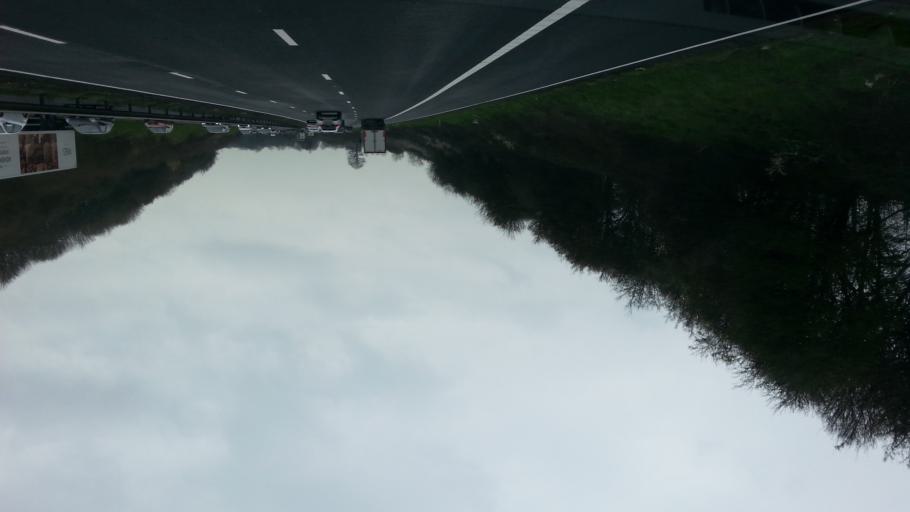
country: GB
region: England
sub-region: Gloucestershire
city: Dursley
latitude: 51.7023
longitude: -2.3899
